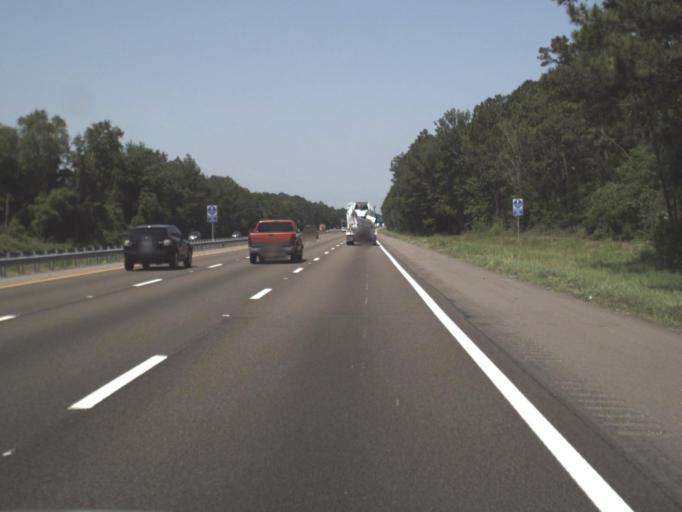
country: US
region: Florida
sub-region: Duval County
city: Baldwin
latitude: 30.3116
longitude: -81.8244
